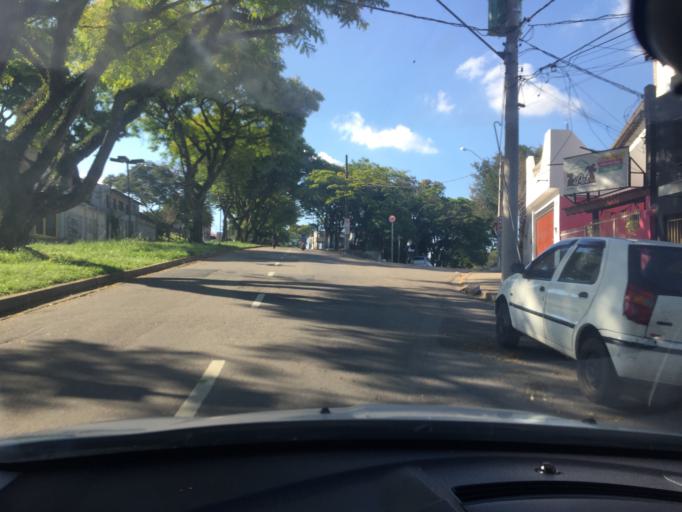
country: BR
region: Sao Paulo
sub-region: Jundiai
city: Jundiai
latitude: -23.2112
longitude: -46.8647
